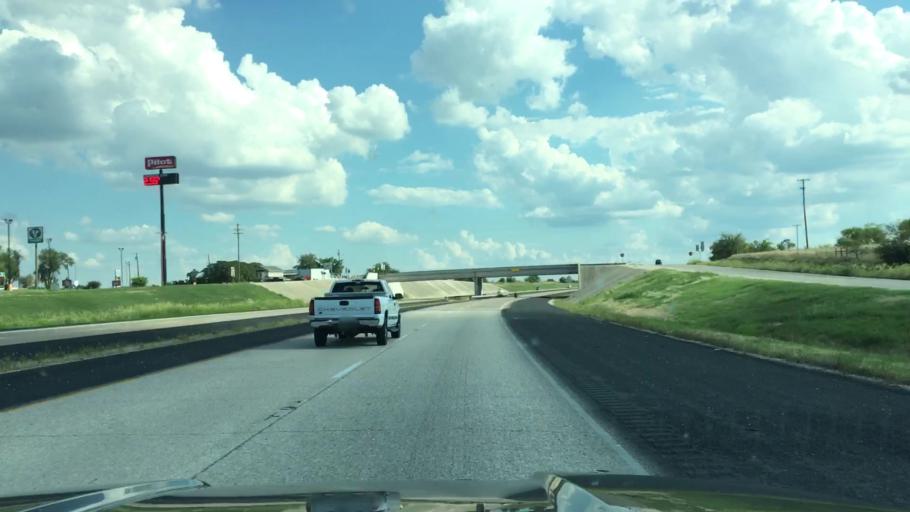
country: US
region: Texas
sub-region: Wise County
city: New Fairview
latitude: 33.1022
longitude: -97.4718
